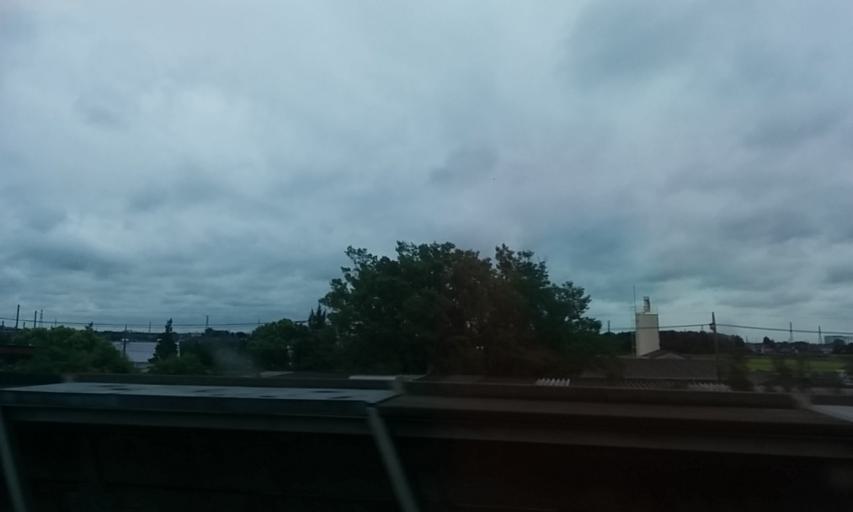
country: JP
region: Saitama
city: Kukichuo
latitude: 36.0852
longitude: 139.6900
